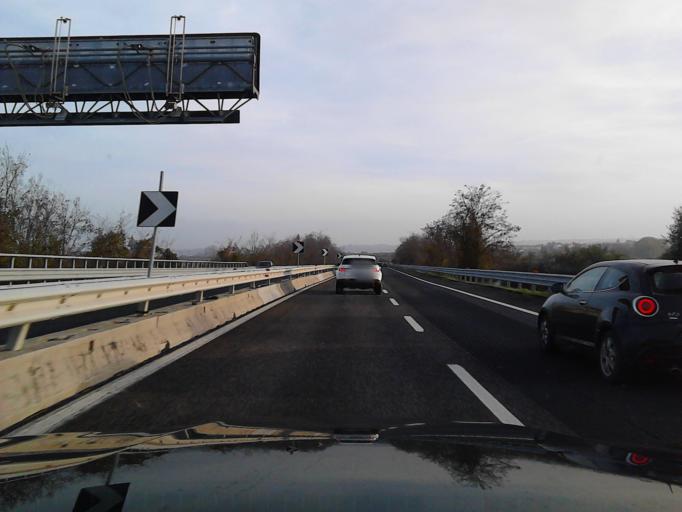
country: IT
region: Abruzzo
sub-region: Provincia di Chieti
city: Ortona
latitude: 42.3210
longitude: 14.3975
